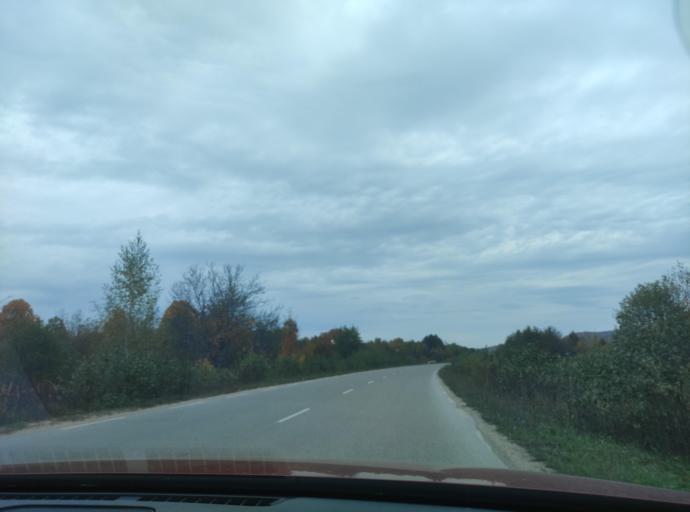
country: BG
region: Montana
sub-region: Obshtina Berkovitsa
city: Berkovitsa
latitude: 43.2352
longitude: 23.1594
